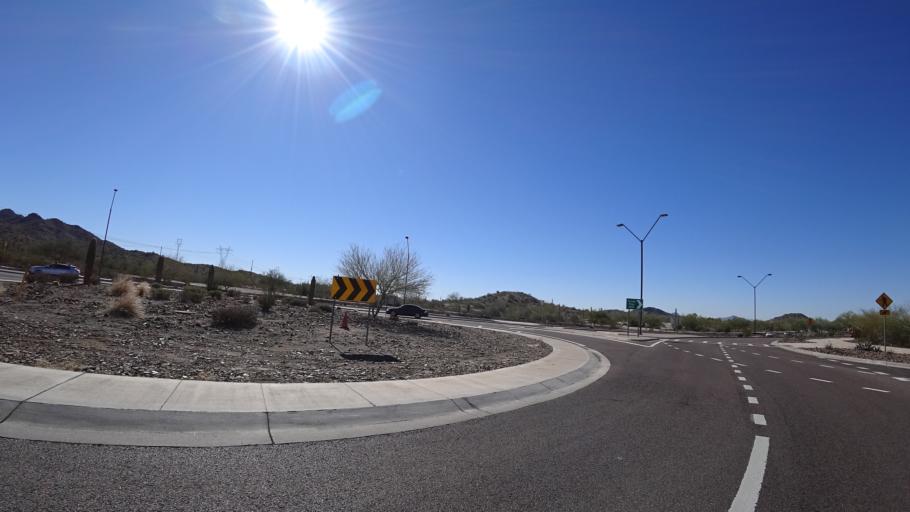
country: US
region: Arizona
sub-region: Maricopa County
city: Goodyear
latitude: 33.3582
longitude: -112.4221
